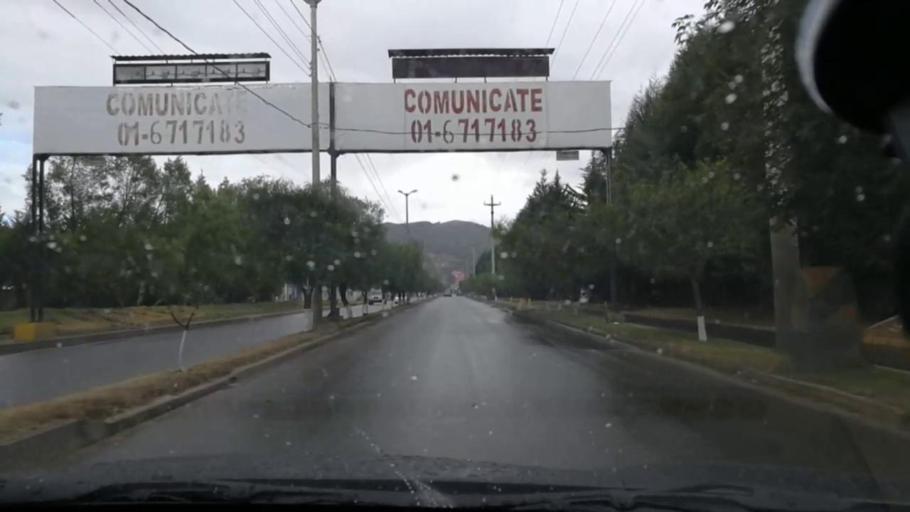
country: PE
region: Cajamarca
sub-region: Provincia de Cajamarca
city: Cajamarca
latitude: -7.1651
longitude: -78.4782
